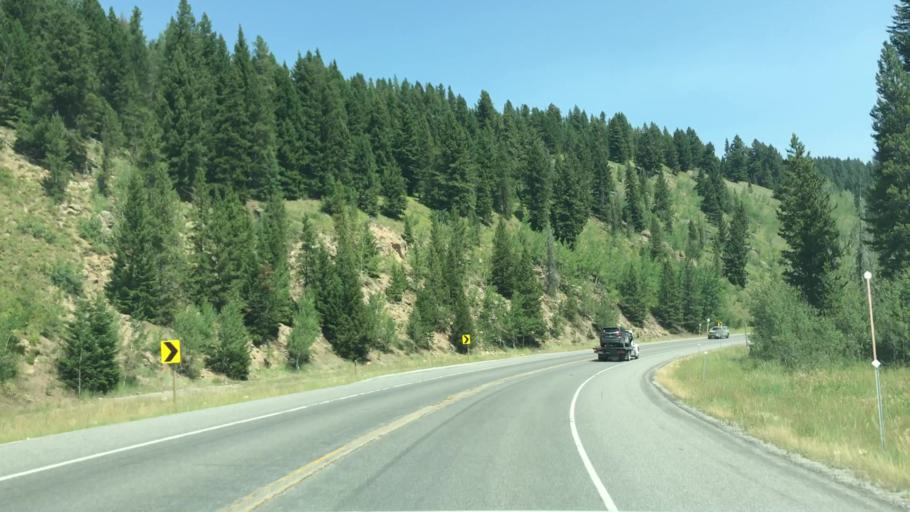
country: US
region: Montana
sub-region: Gallatin County
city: West Yellowstone
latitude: 44.8033
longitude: -111.1090
